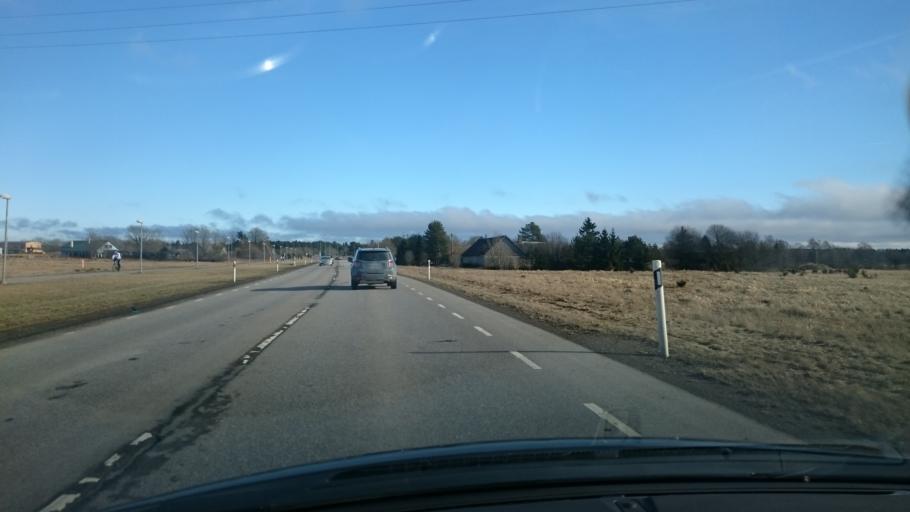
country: EE
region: Harju
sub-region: Harku vald
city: Tabasalu
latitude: 59.4433
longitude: 24.4860
